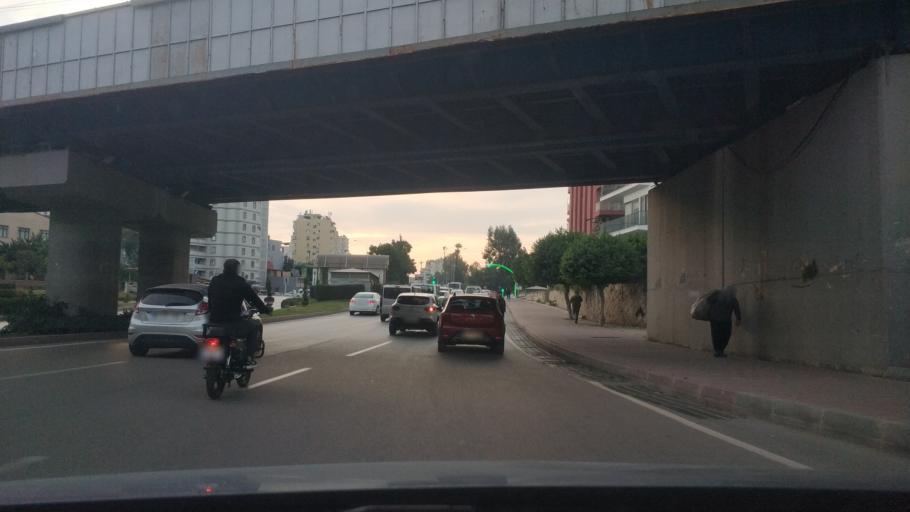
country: TR
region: Adana
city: Adana
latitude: 37.0029
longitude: 35.3124
